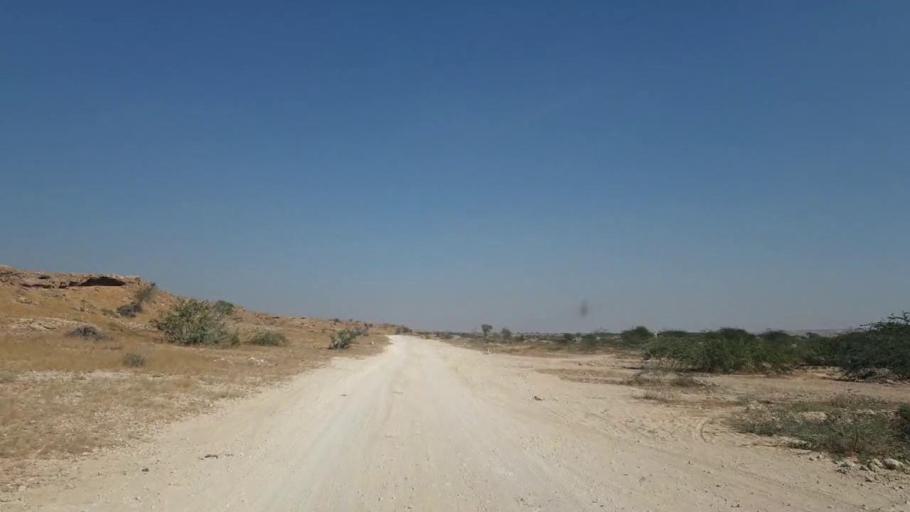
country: PK
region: Sindh
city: Thatta
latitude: 25.2187
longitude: 67.7964
